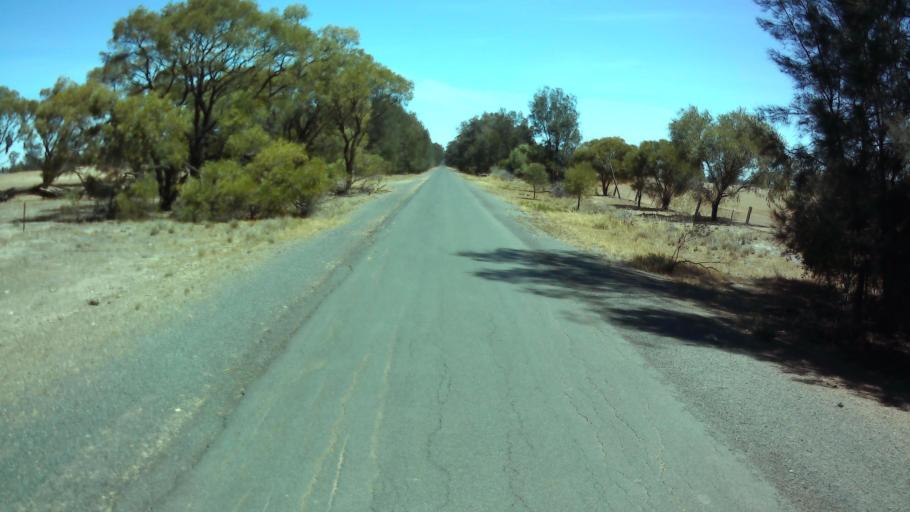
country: AU
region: New South Wales
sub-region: Weddin
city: Grenfell
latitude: -33.8752
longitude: 147.6913
